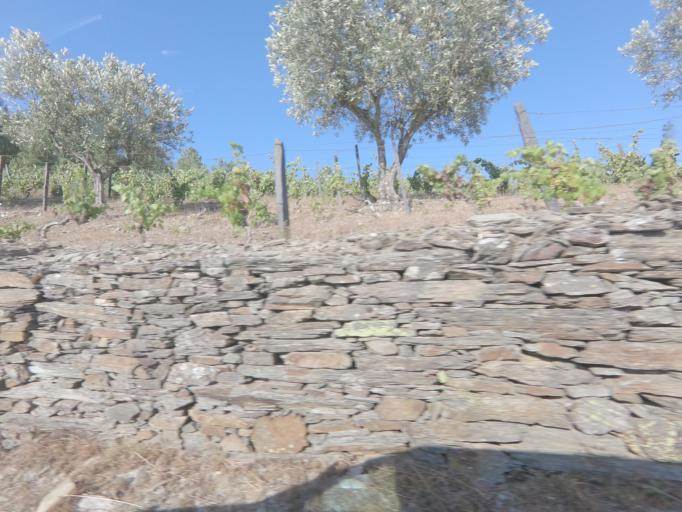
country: PT
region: Vila Real
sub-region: Sabrosa
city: Vilela
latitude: 41.1738
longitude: -7.5943
